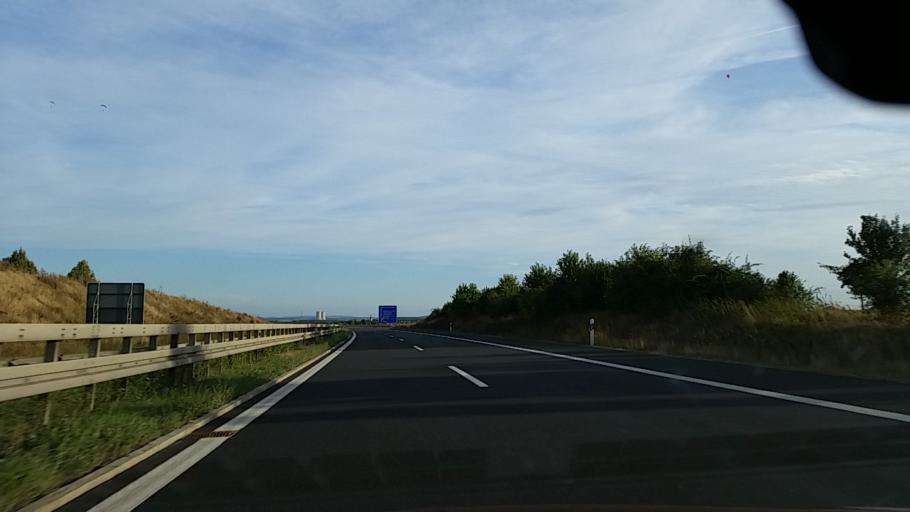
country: DE
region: Bavaria
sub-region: Regierungsbezirk Unterfranken
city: Euerbach
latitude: 50.0680
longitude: 10.1469
